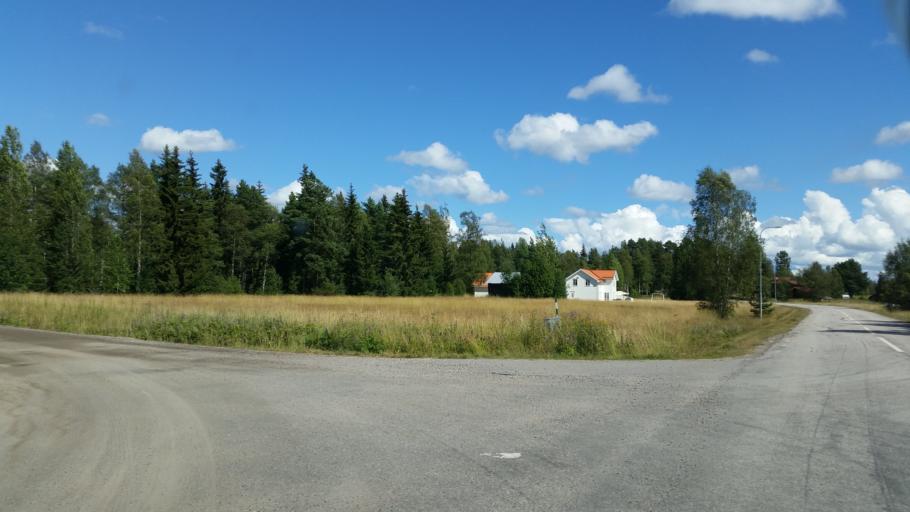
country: SE
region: Gaevleborg
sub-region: Ljusdals Kommun
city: Ljusdal
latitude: 61.8387
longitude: 16.1237
